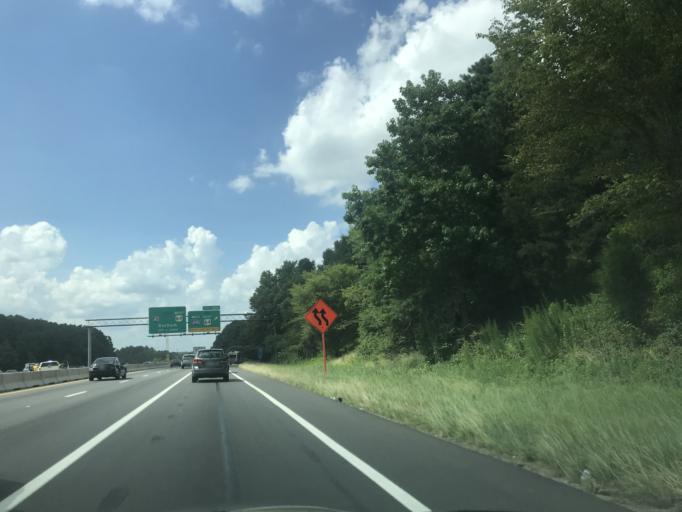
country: US
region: North Carolina
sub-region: Wake County
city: Garner
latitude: 35.7481
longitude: -78.5936
